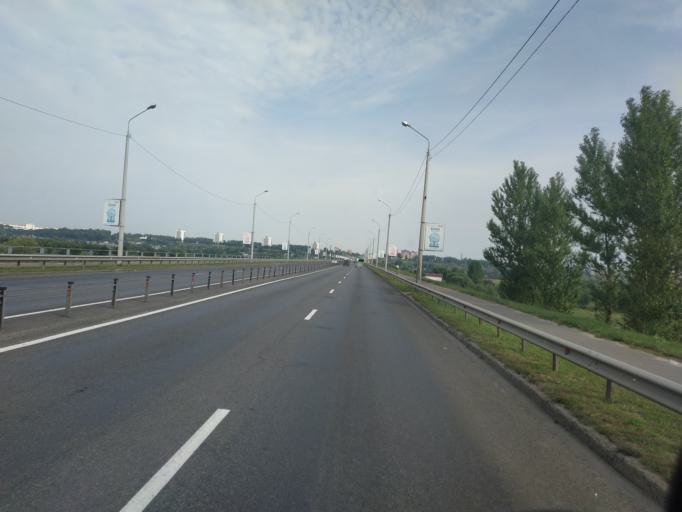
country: BY
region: Mogilev
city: Mahilyow
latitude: 53.8870
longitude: 30.3782
